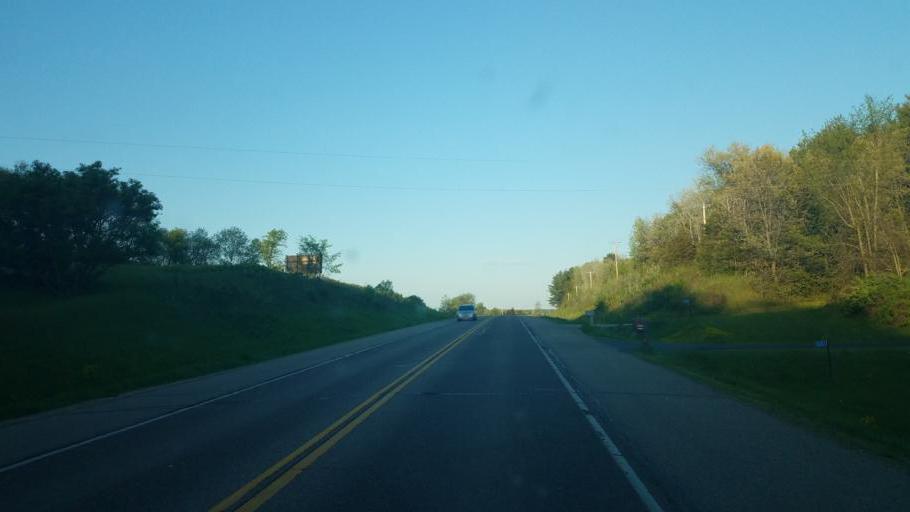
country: US
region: Wisconsin
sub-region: Sauk County
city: Reedsburg
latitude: 43.5331
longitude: -89.9067
